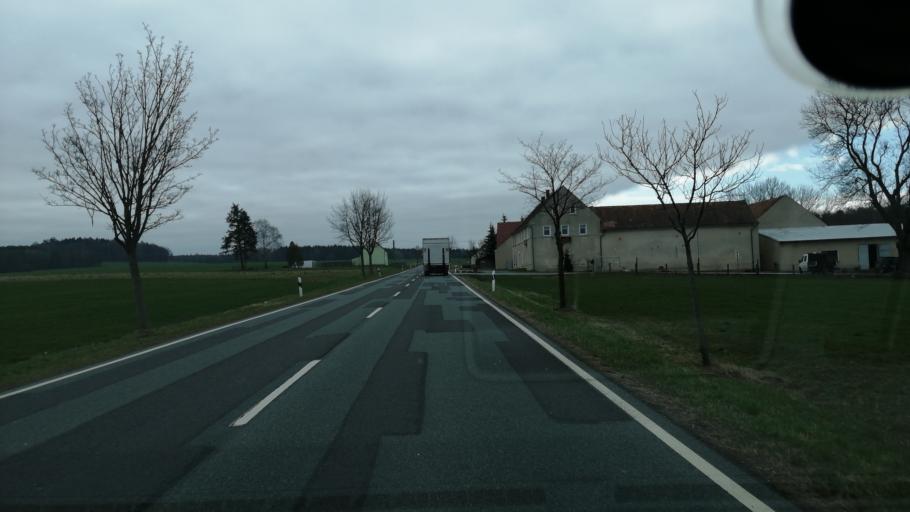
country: DE
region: Saxony
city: Niedercunnersdorf
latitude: 51.0595
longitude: 14.6949
